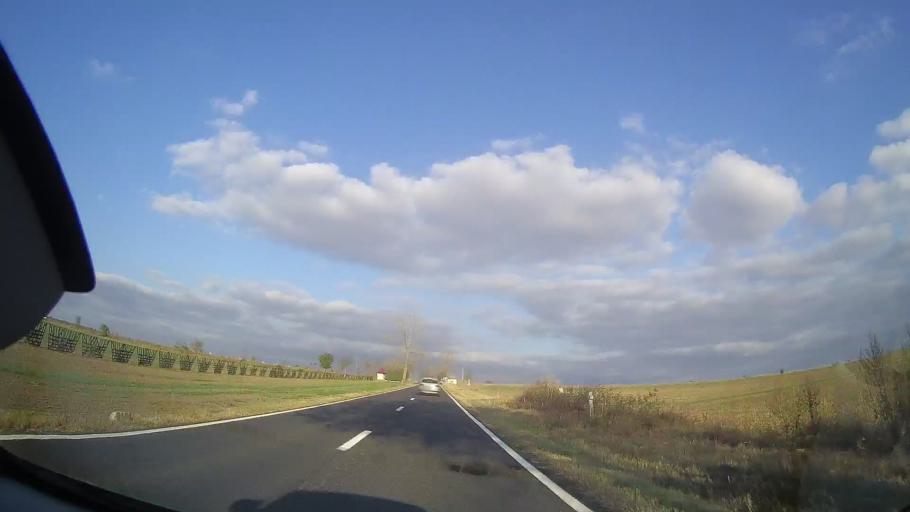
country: RO
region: Tulcea
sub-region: Comuna Topolog
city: Topolog
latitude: 44.8462
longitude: 28.3156
